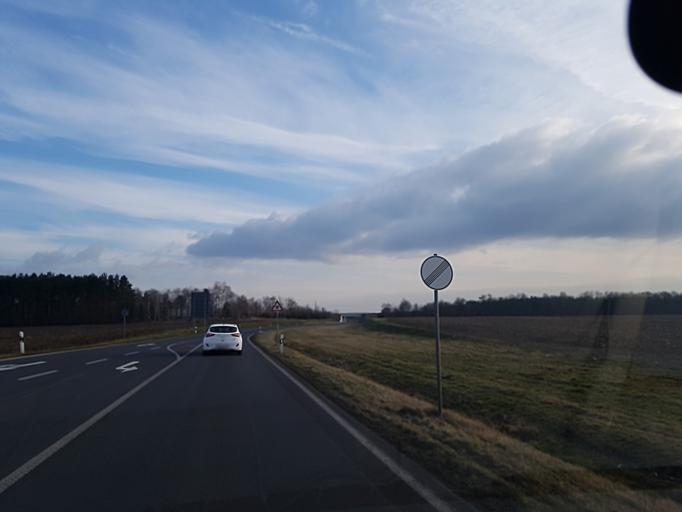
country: DE
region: Brandenburg
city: Belzig
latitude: 52.1463
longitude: 12.6202
